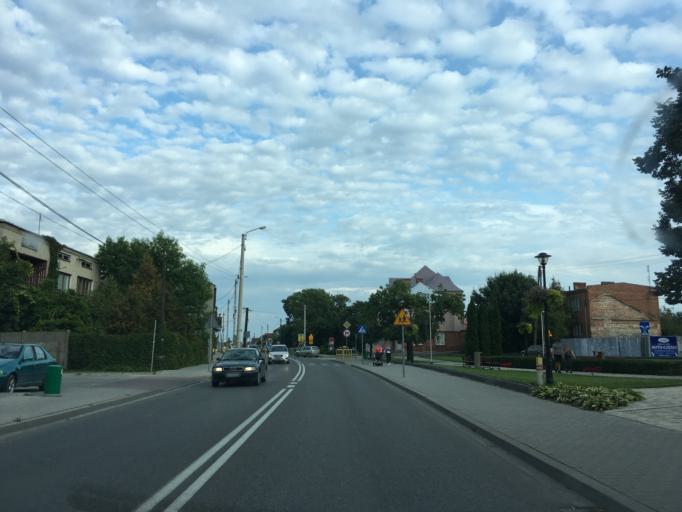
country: PL
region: Swietokrzyskie
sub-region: Powiat wloszczowski
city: Wloszczowa
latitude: 50.8518
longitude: 19.9698
